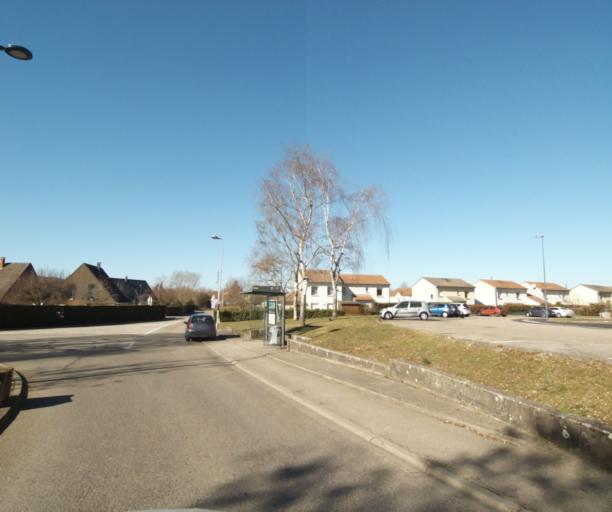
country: FR
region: Lorraine
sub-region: Departement de Meurthe-et-Moselle
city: Heillecourt
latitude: 48.6481
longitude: 6.2066
